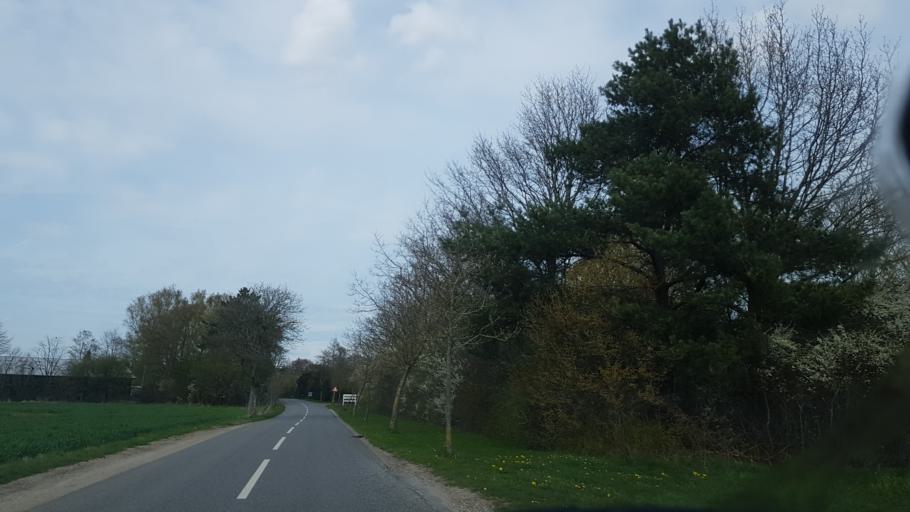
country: DK
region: Capital Region
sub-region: Allerod Kommune
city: Lynge
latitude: 55.8628
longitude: 12.2935
